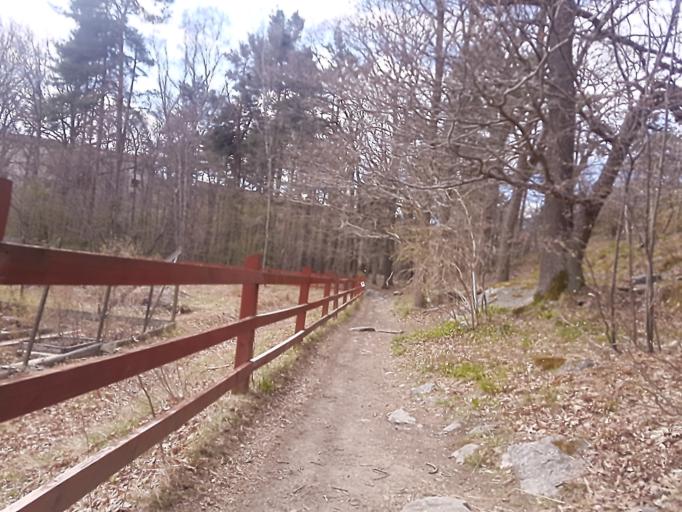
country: SE
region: Stockholm
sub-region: Stockholms Kommun
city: OEstermalm
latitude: 59.2982
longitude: 18.1113
